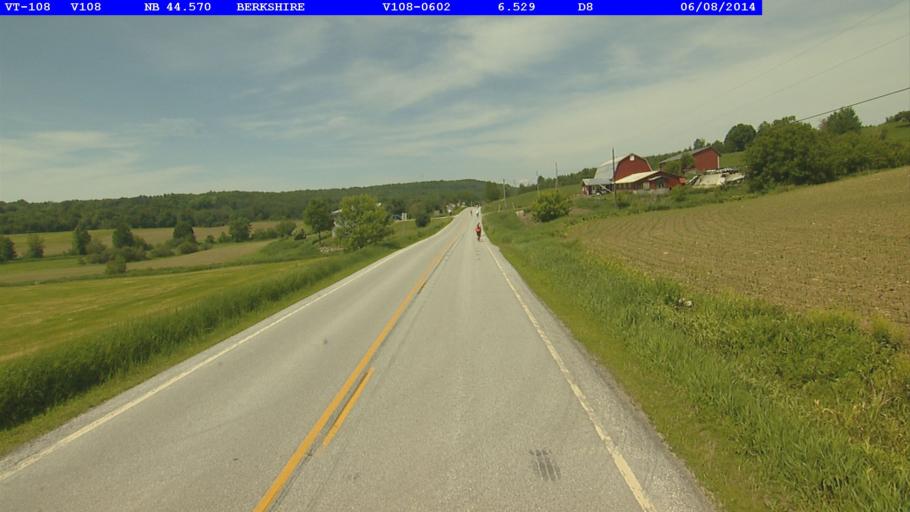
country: US
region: Vermont
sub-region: Franklin County
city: Enosburg Falls
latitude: 45.0110
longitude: -72.8248
